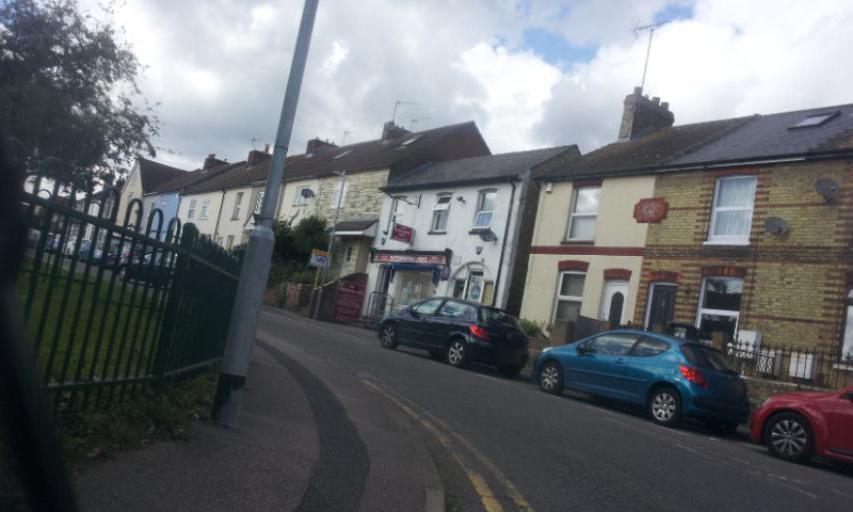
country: GB
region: England
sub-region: Kent
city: Snodland
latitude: 51.3306
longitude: 0.4402
